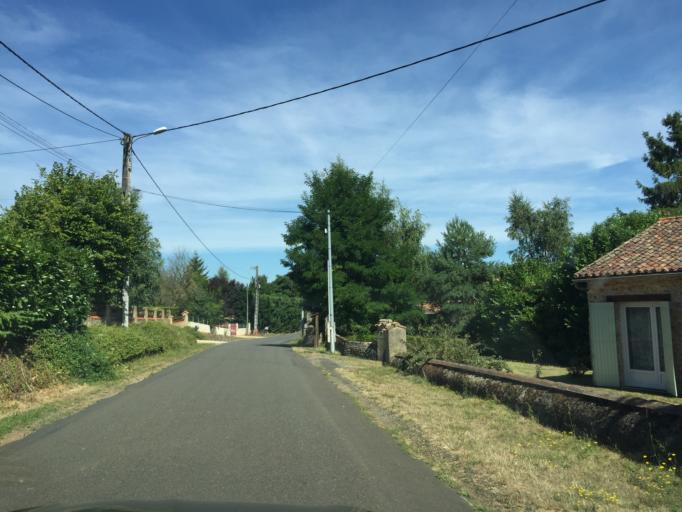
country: FR
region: Poitou-Charentes
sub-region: Departement de la Vienne
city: Iteuil
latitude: 46.4604
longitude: 0.3201
